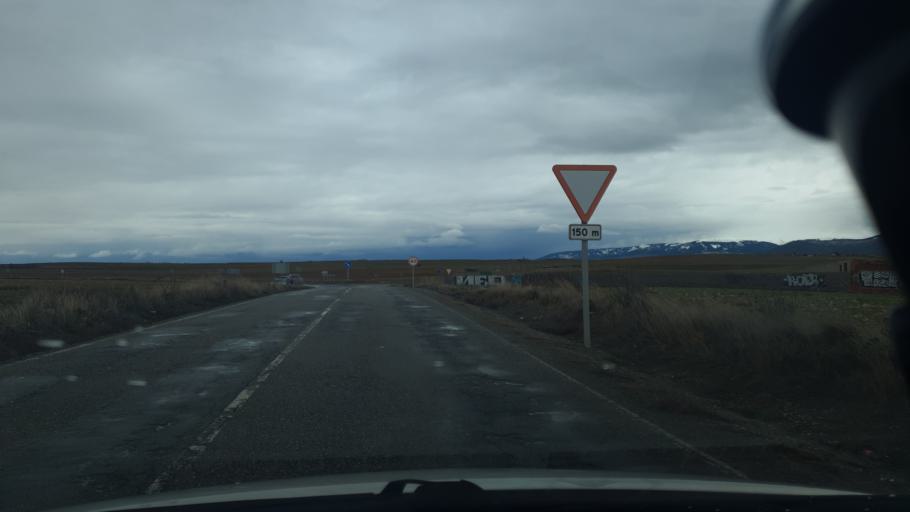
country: ES
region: Castille and Leon
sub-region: Provincia de Segovia
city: Segovia
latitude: 40.9696
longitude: -4.1371
